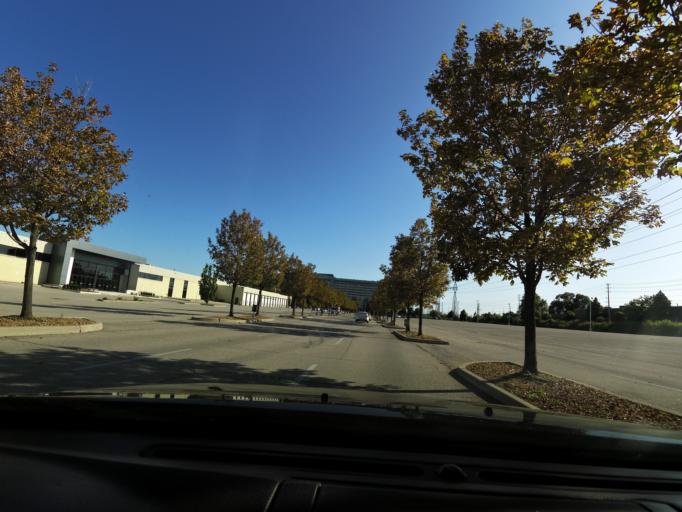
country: CA
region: Ontario
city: Etobicoke
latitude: 43.6926
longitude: -79.5802
